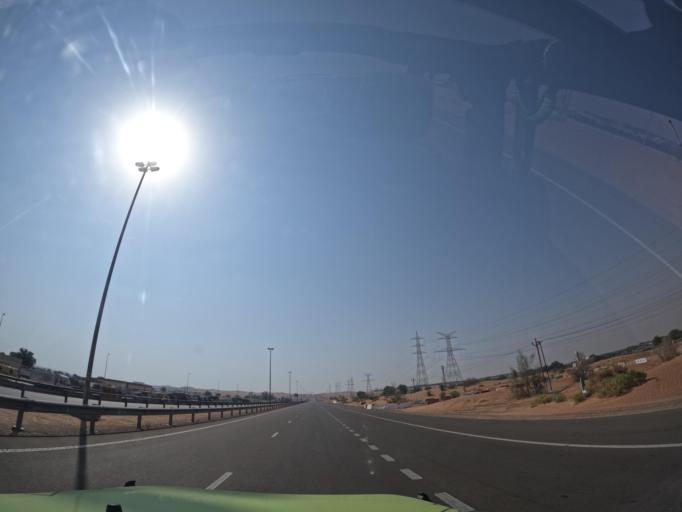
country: OM
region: Al Buraimi
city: Al Buraymi
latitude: 24.3622
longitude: 55.7308
